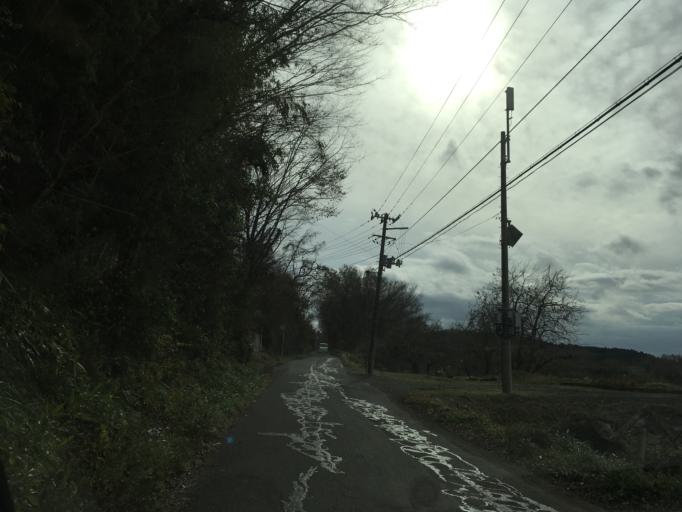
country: JP
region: Iwate
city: Ichinoseki
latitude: 38.7641
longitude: 141.2748
